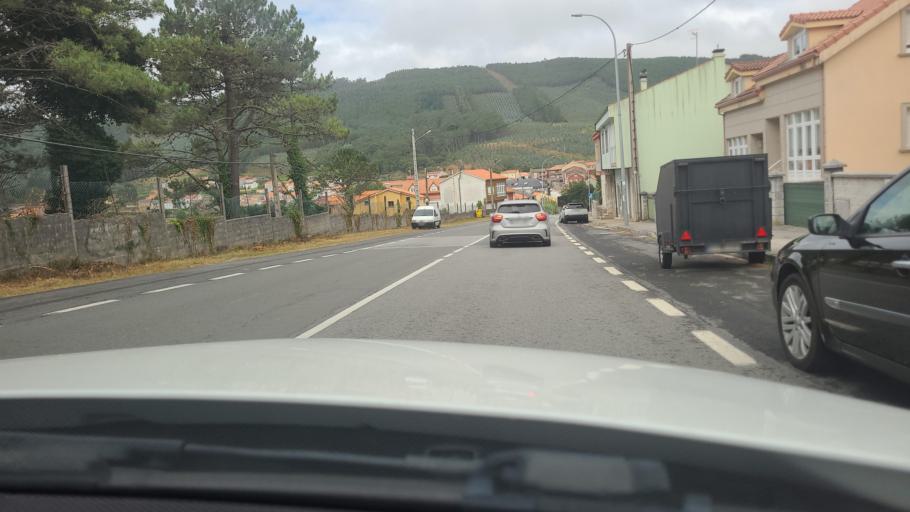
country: ES
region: Galicia
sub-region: Provincia da Coruna
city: Corcubion
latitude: 42.9429
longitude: -9.2279
